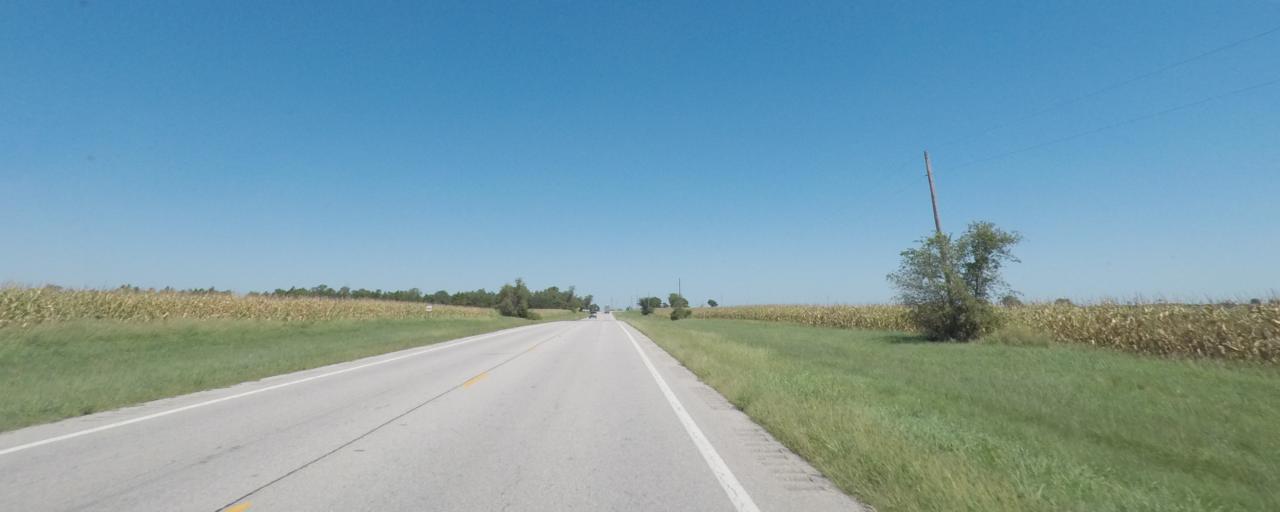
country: US
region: Kansas
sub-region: Sumner County
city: Belle Plaine
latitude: 37.3841
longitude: -97.3850
